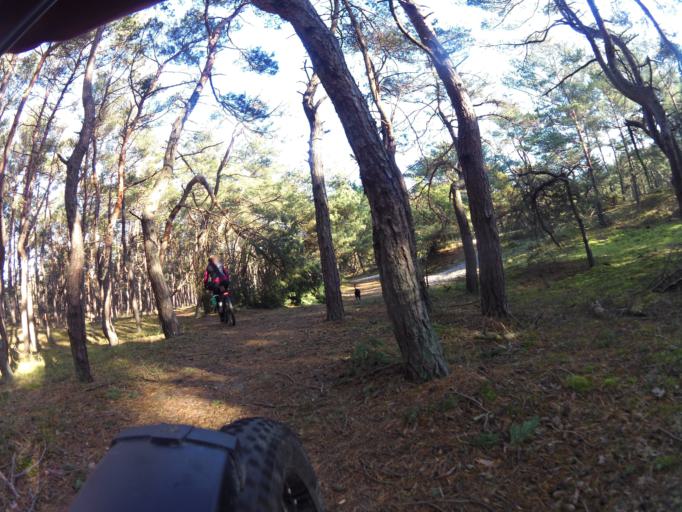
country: PL
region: Pomeranian Voivodeship
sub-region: Powiat pucki
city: Hel
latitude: 54.6049
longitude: 18.8220
